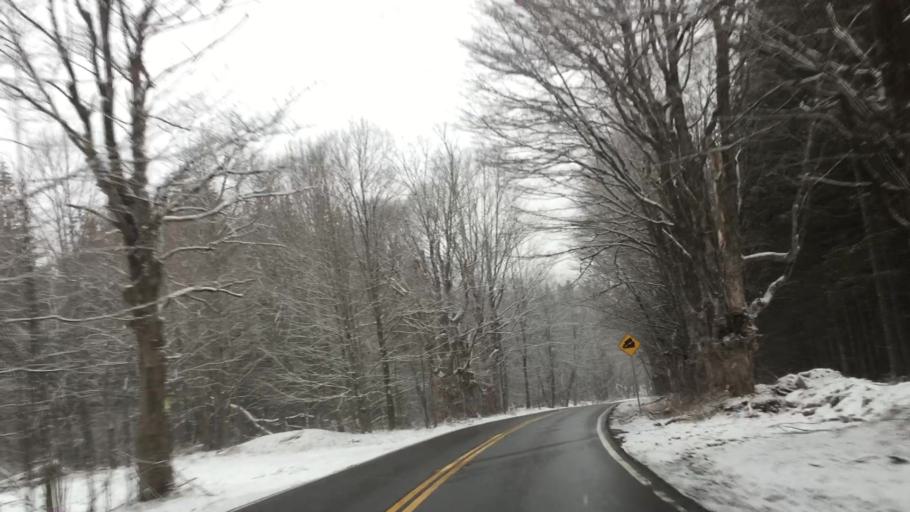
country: US
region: Massachusetts
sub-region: Berkshire County
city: Hinsdale
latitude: 42.4102
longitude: -73.1820
